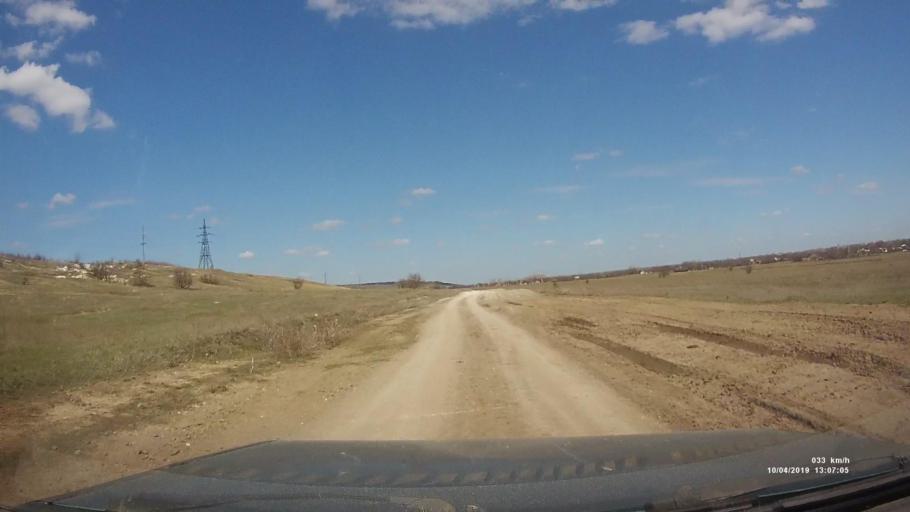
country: RU
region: Rostov
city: Masalovka
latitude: 48.3941
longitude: 40.2387
